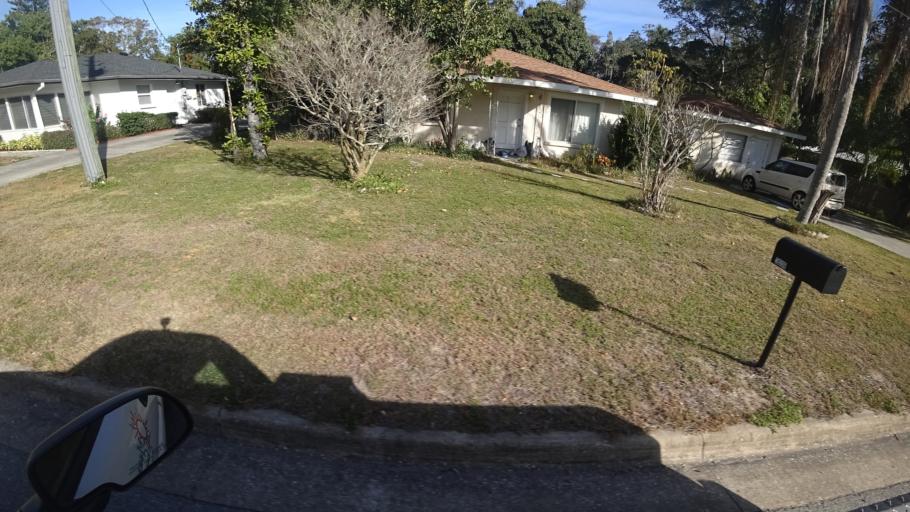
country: US
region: Florida
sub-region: Manatee County
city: Bradenton
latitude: 27.4846
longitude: -82.5820
